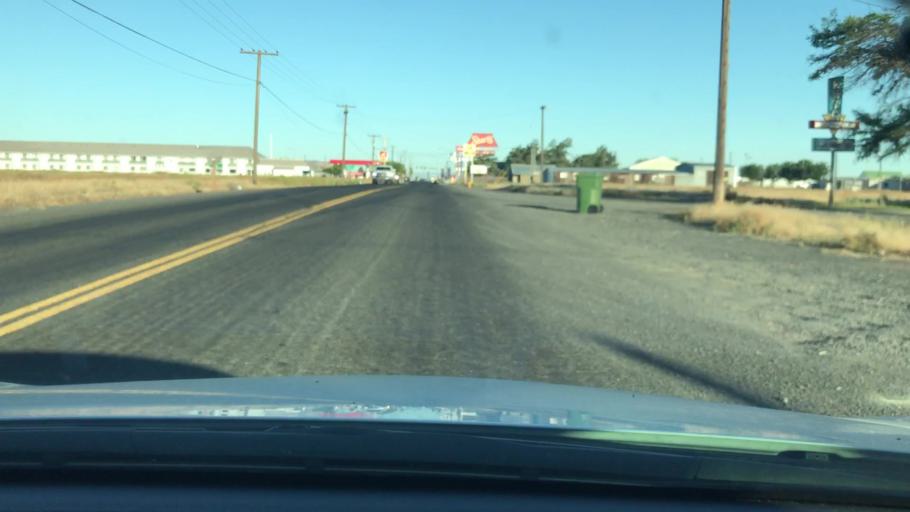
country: US
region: Washington
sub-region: Grant County
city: Moses Lake
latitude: 47.1017
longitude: -119.2407
